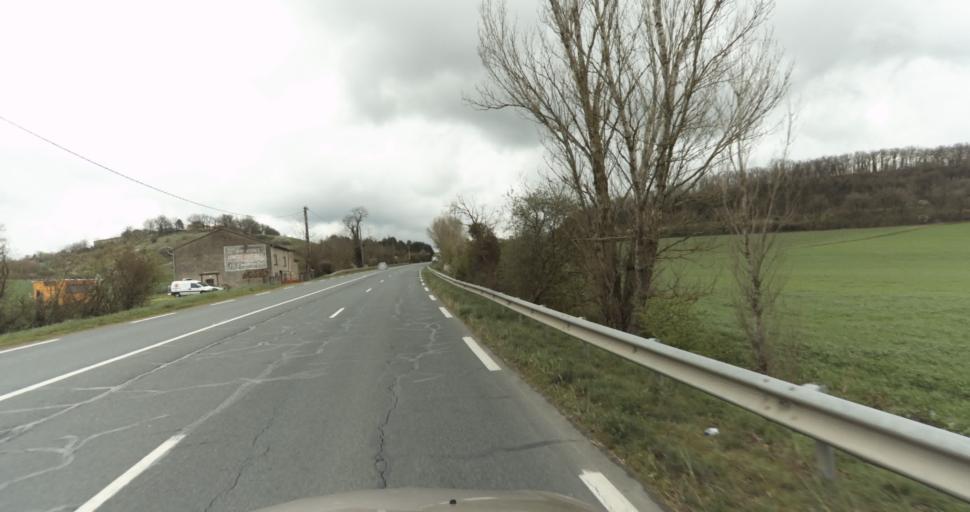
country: FR
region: Midi-Pyrenees
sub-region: Departement du Tarn
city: Puygouzon
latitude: 43.8694
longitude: 2.1842
